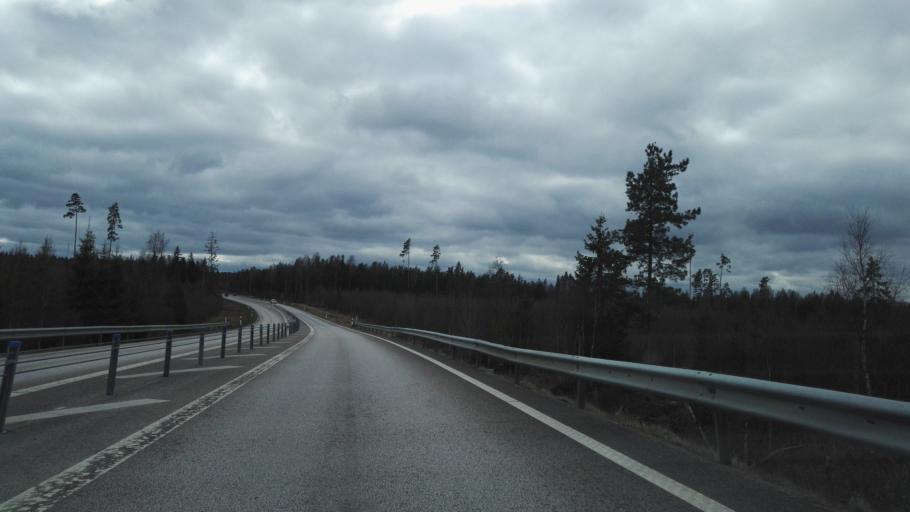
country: SE
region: Kronoberg
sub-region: Alvesta Kommun
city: Vislanda
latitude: 56.7469
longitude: 14.5123
